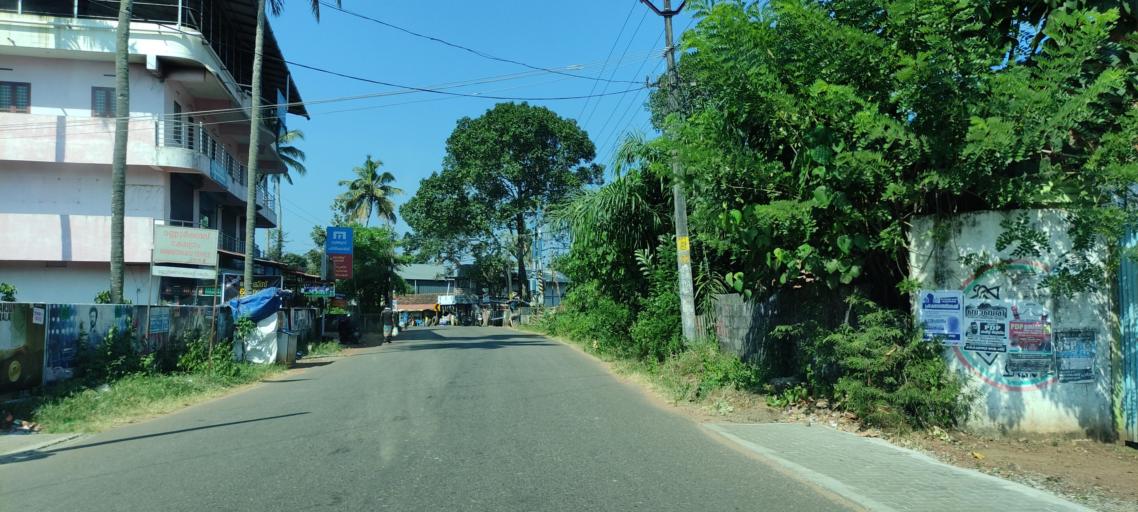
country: IN
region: Kerala
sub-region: Kollam
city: Panmana
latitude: 9.0430
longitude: 76.5814
